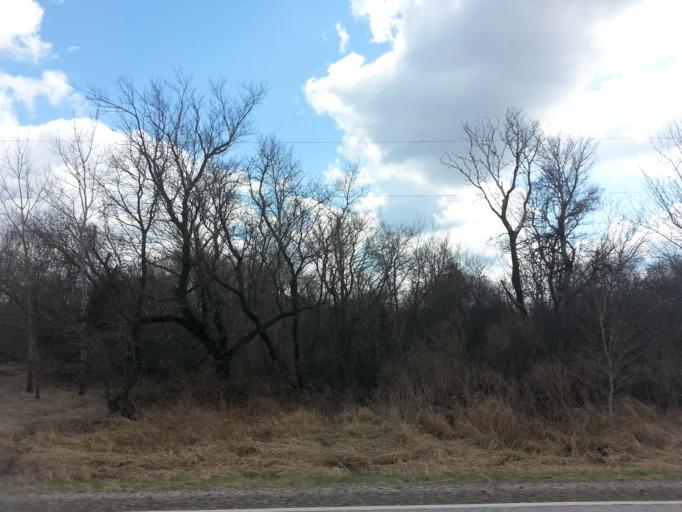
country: US
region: Minnesota
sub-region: Dodge County
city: Mantorville
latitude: 44.0944
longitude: -92.7107
